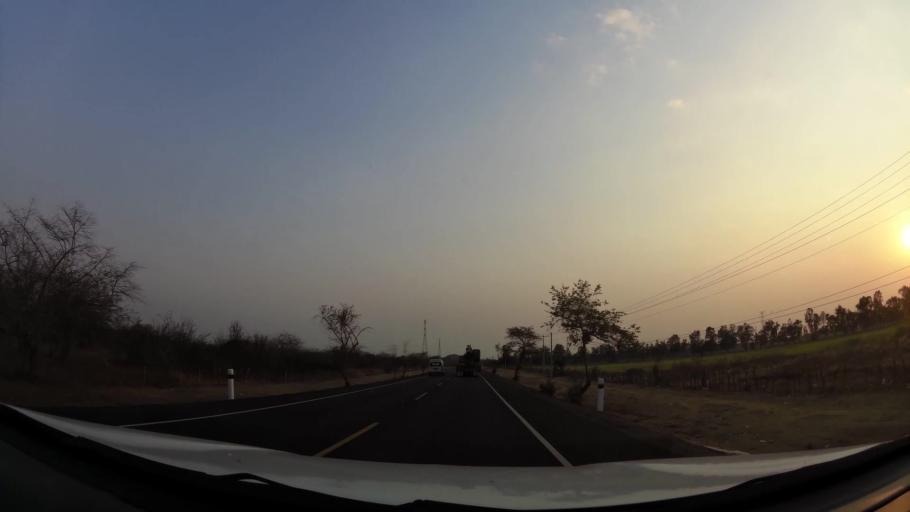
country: NI
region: Leon
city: La Paz Centro
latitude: 12.3235
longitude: -86.6902
